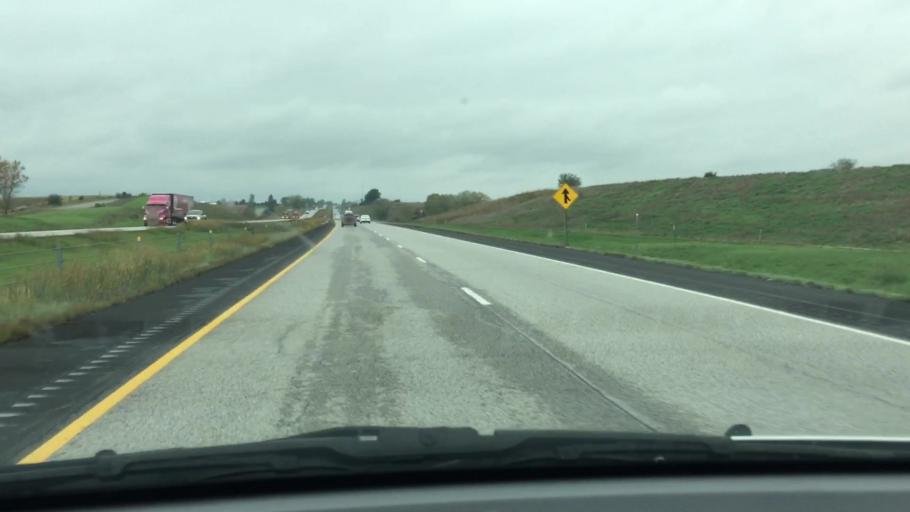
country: US
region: Iowa
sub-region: Johnson County
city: Tiffin
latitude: 41.6879
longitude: -91.8063
